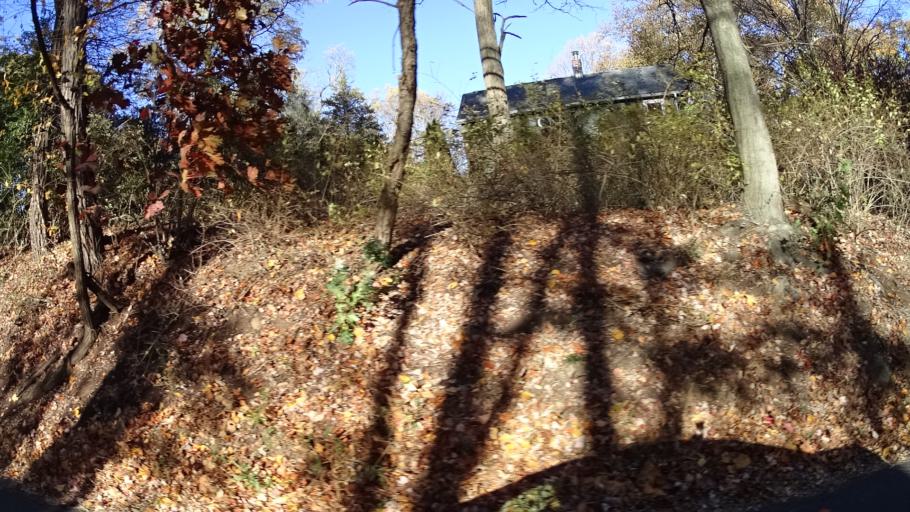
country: US
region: New Jersey
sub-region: Union County
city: Mountainside
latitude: 40.6767
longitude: -74.3649
